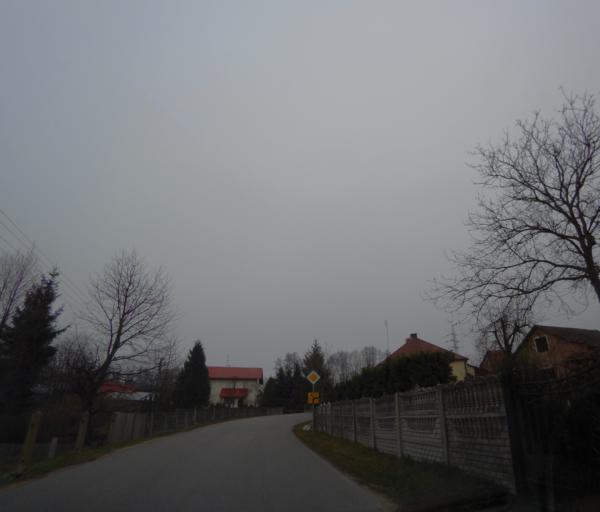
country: PL
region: Subcarpathian Voivodeship
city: Nowa Sarzyna
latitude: 50.2889
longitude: 22.3538
